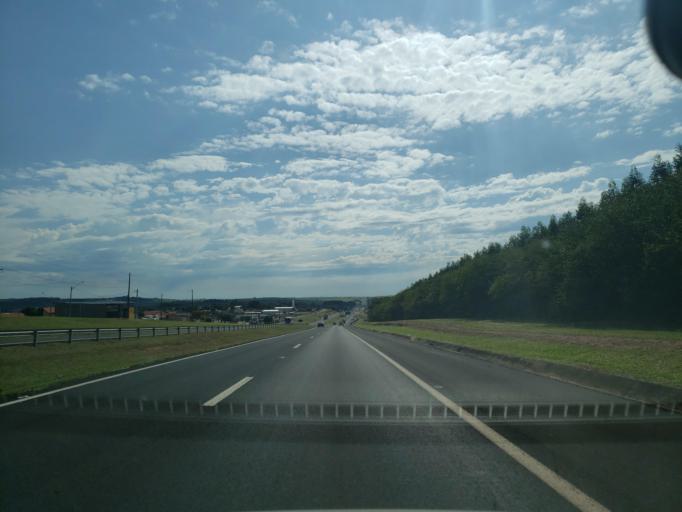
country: BR
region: Sao Paulo
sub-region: Pirajui
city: Pirajui
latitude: -21.9967
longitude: -49.4344
